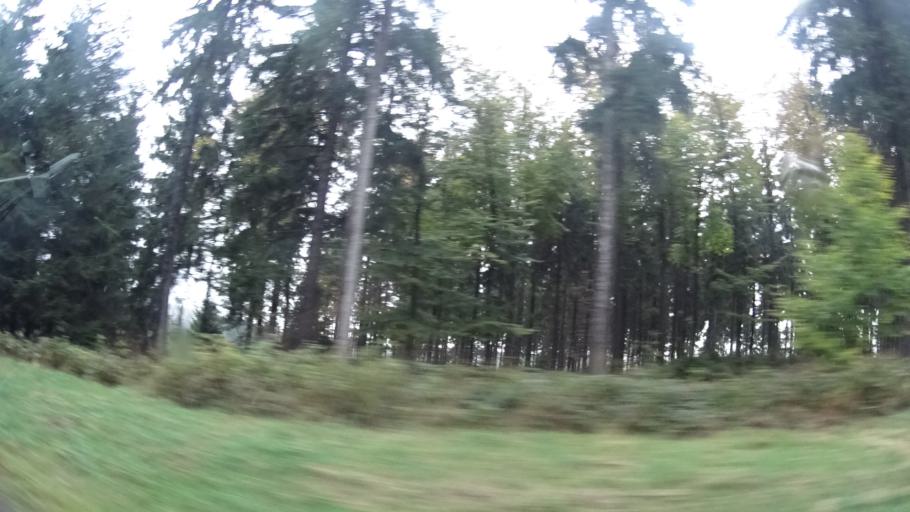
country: DE
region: Bavaria
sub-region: Upper Franconia
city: Tschirn
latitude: 50.4298
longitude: 11.4636
